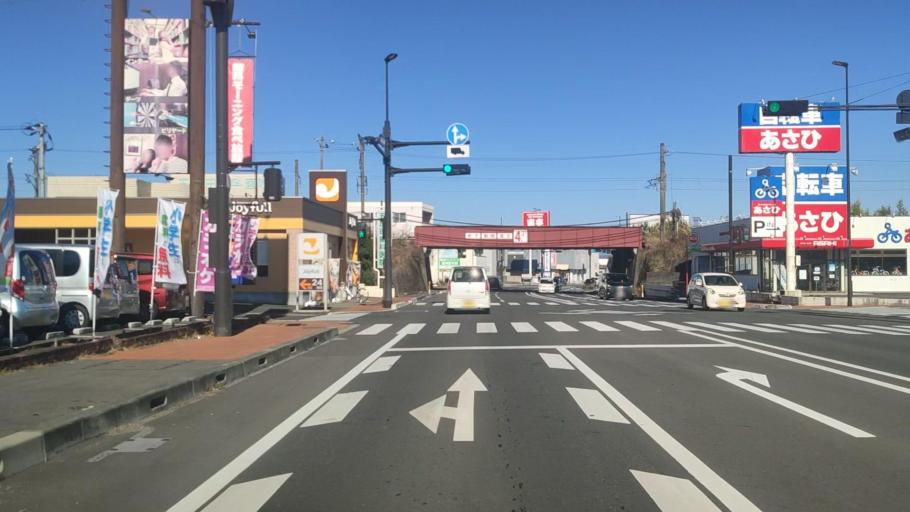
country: JP
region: Miyazaki
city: Miyakonojo
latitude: 31.7363
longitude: 131.0691
